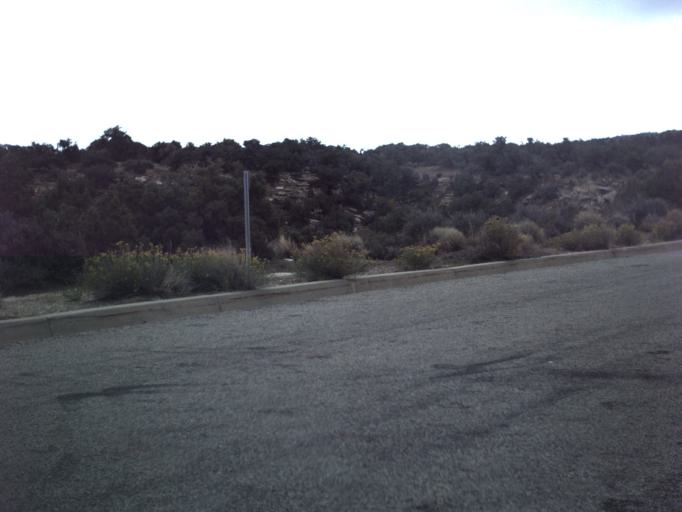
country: US
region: Utah
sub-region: Emery County
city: Ferron
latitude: 38.8615
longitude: -110.8115
